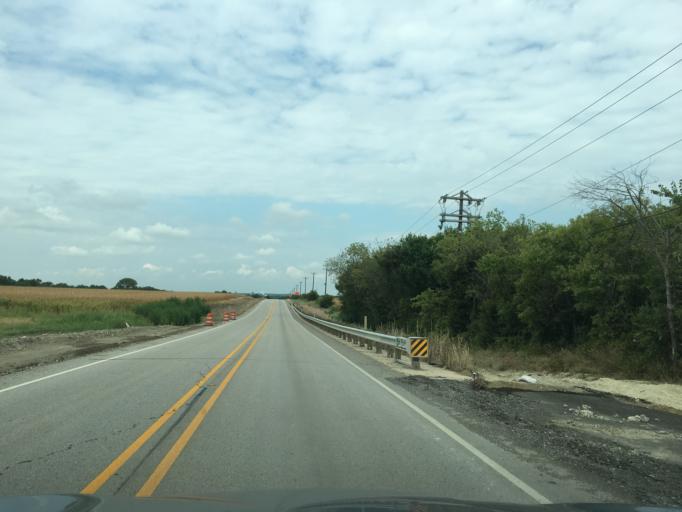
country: US
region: Texas
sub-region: Collin County
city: Anna
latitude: 33.3455
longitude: -96.5928
